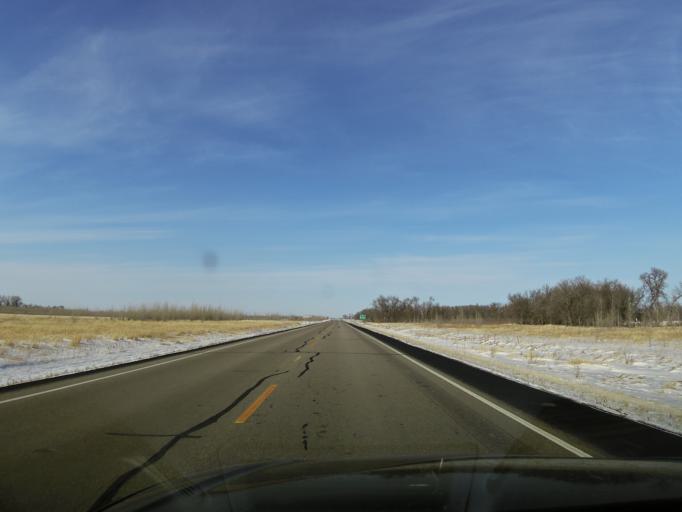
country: US
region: North Dakota
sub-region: Walsh County
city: Grafton
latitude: 48.4091
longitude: -97.1072
